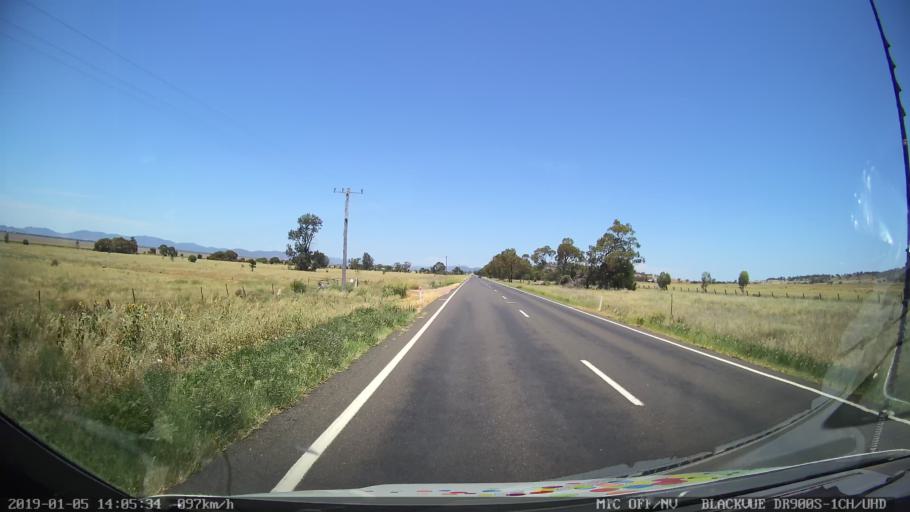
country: AU
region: New South Wales
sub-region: Gunnedah
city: Gunnedah
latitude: -31.2112
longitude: 150.3776
